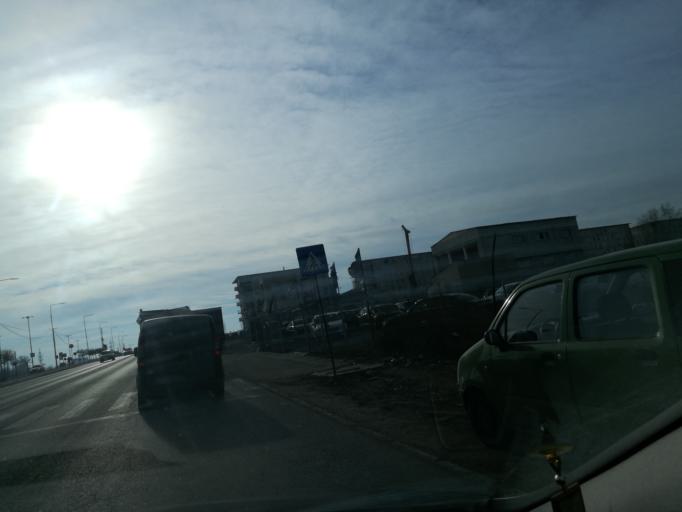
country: RO
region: Constanta
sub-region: Municipiul Constanta
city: Palazu Mare
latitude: 44.2012
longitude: 28.6082
